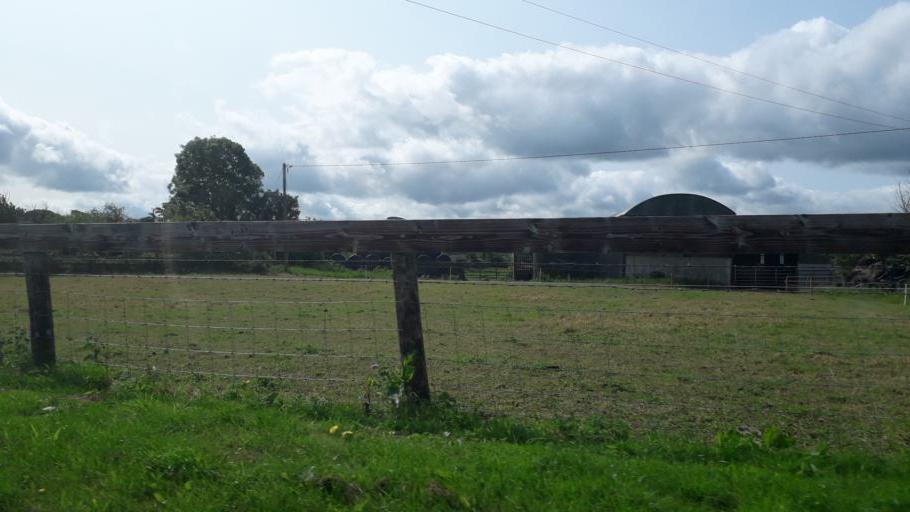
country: IE
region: Leinster
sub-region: Kilkenny
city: Graiguenamanagh
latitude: 52.6050
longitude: -6.9974
